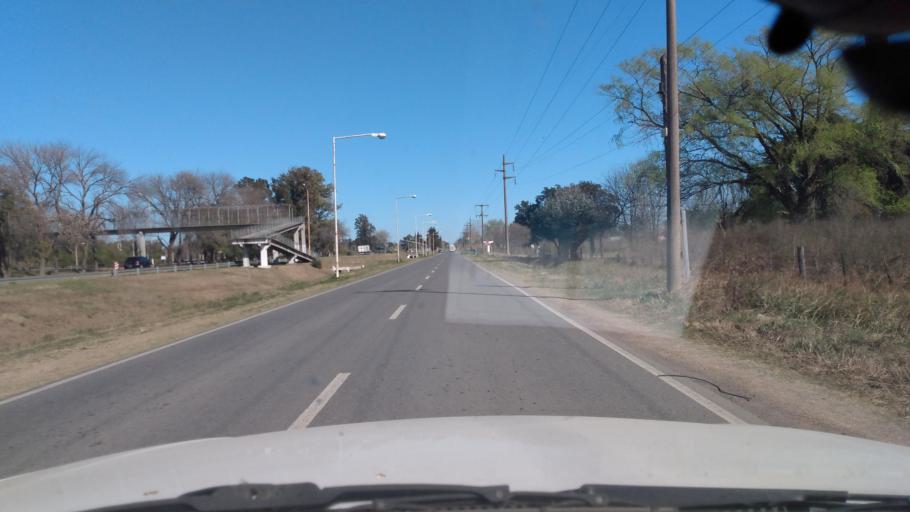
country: AR
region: Buenos Aires
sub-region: Partido de Mercedes
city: Mercedes
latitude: -34.6571
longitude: -59.3612
